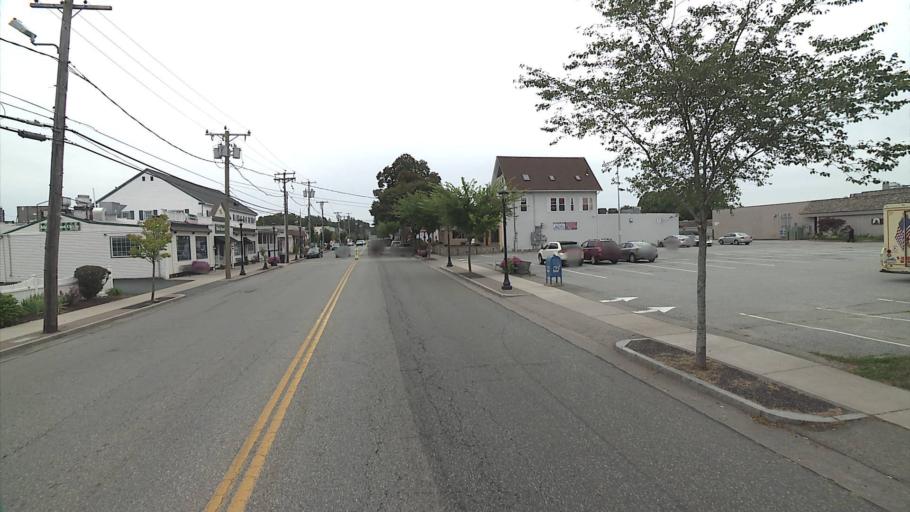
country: US
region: Connecticut
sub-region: New London County
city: Niantic
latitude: 41.3235
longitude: -72.1925
